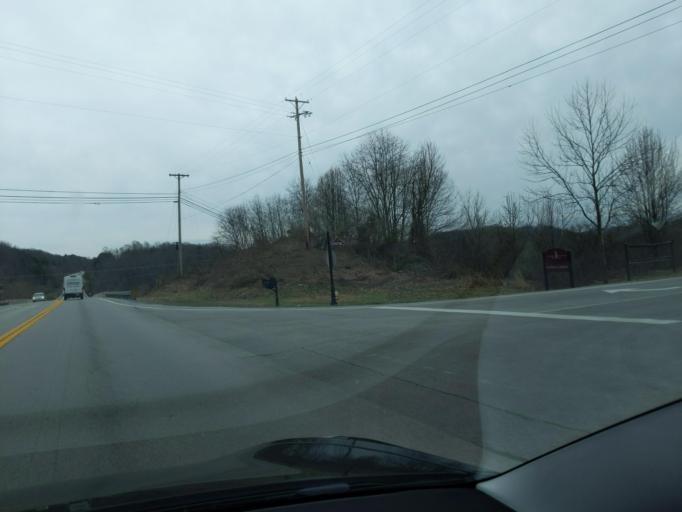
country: US
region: Kentucky
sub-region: Whitley County
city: Corbin
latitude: 36.9166
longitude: -84.0885
